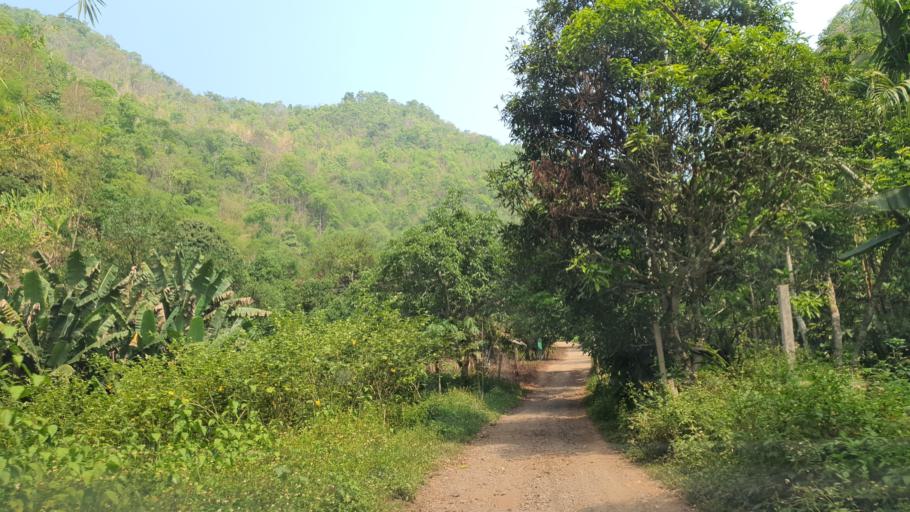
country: TH
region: Chiang Mai
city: Samoeng
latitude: 18.7984
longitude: 98.7956
